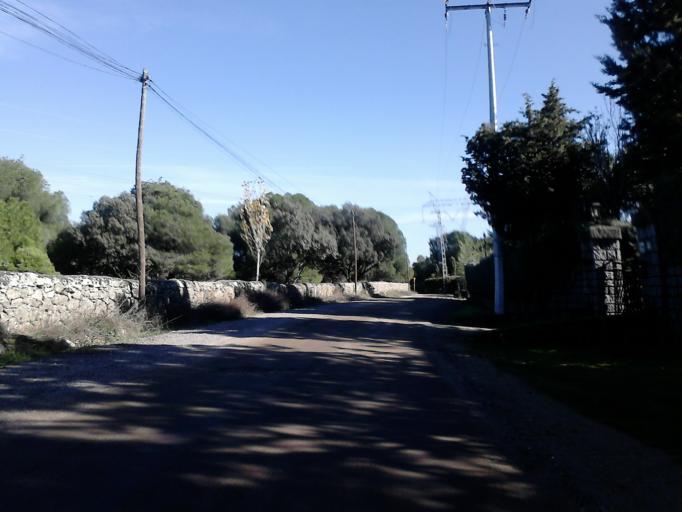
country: ES
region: Madrid
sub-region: Provincia de Madrid
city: Galapagar
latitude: 40.5740
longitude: -3.9822
